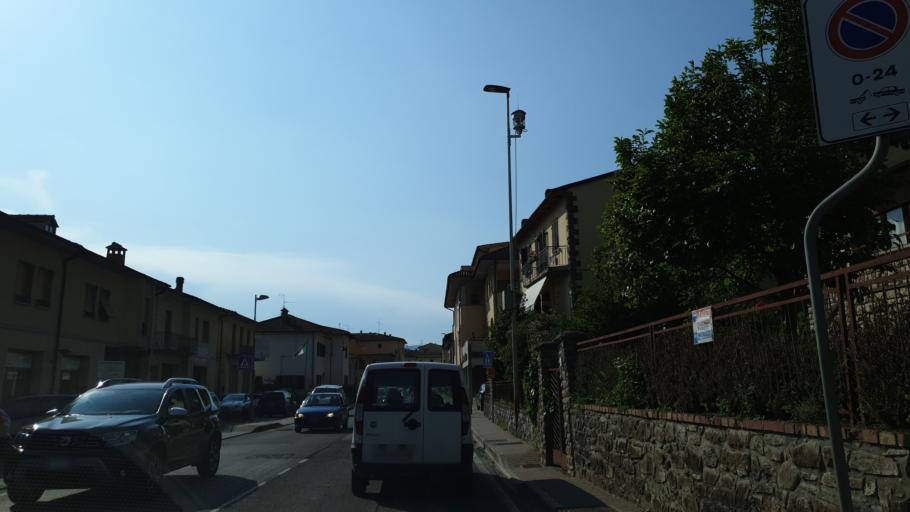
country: IT
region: Tuscany
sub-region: Province of Arezzo
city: Ponte a Poppi
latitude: 43.7275
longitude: 11.7705
